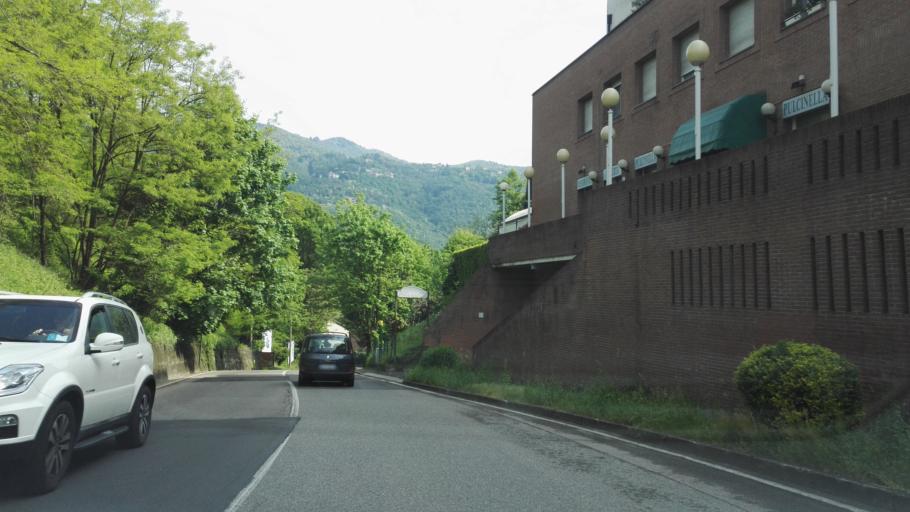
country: IT
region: Lombardy
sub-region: Provincia di Como
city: Como
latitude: 45.7947
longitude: 9.0984
